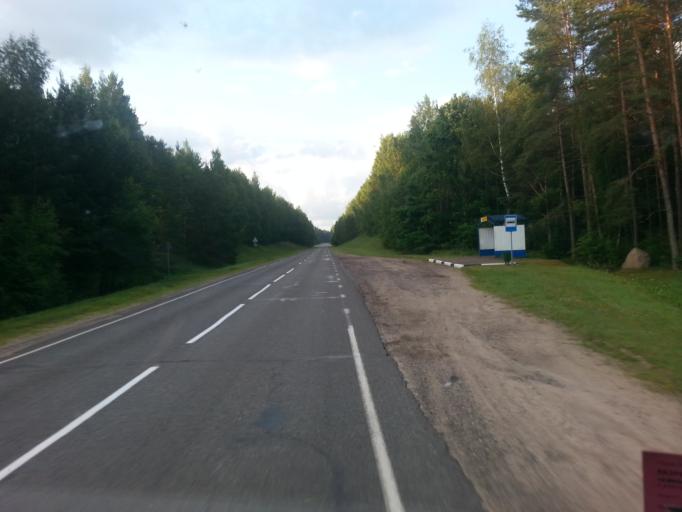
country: BY
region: Minsk
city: Kryvichy
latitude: 54.6044
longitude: 27.1833
